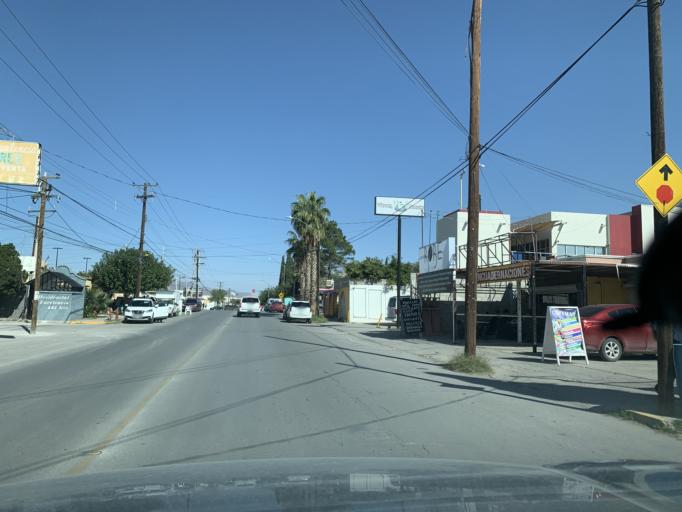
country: MX
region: Chihuahua
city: Ciudad Juarez
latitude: 31.7412
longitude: -106.4335
